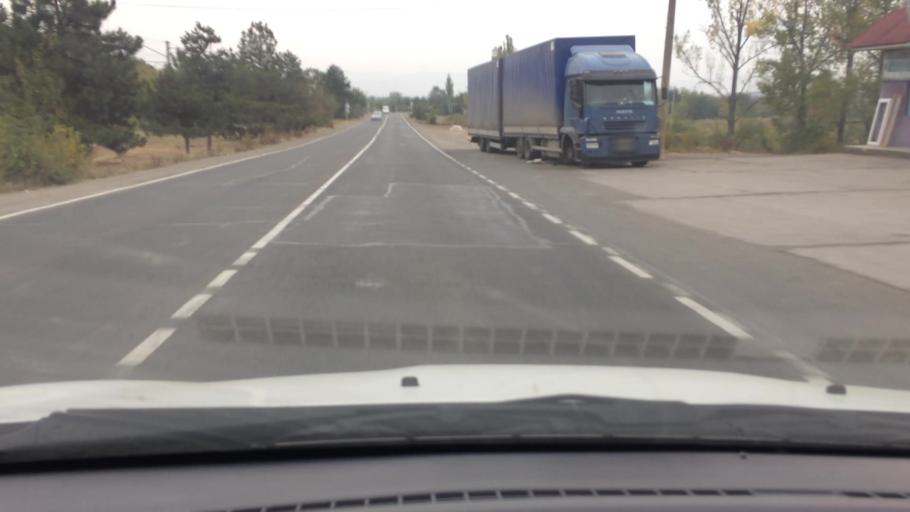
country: GE
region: Kvemo Kartli
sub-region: Marneuli
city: Marneuli
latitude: 41.4125
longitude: 44.8294
